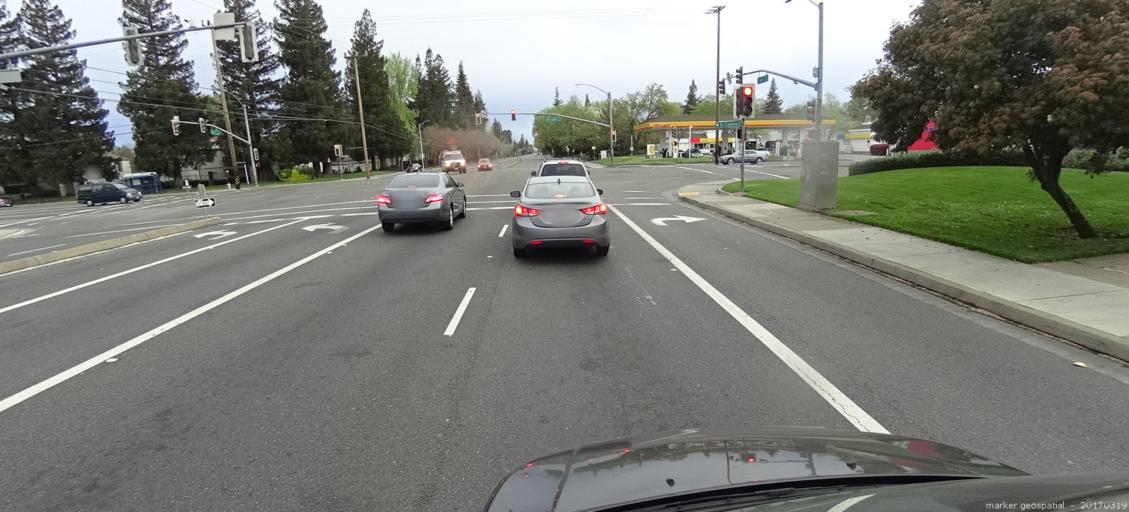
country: US
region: California
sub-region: Sacramento County
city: Sacramento
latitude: 38.6123
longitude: -121.4978
